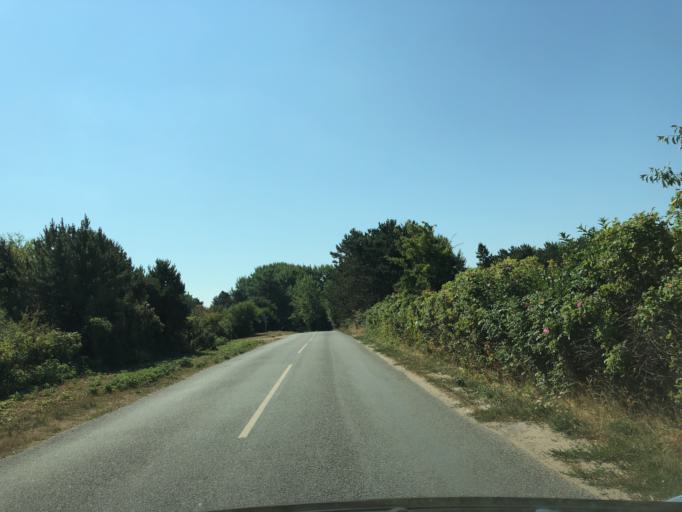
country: DK
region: Zealand
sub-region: Odsherred Kommune
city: Asnaes
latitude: 55.9886
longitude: 11.2976
